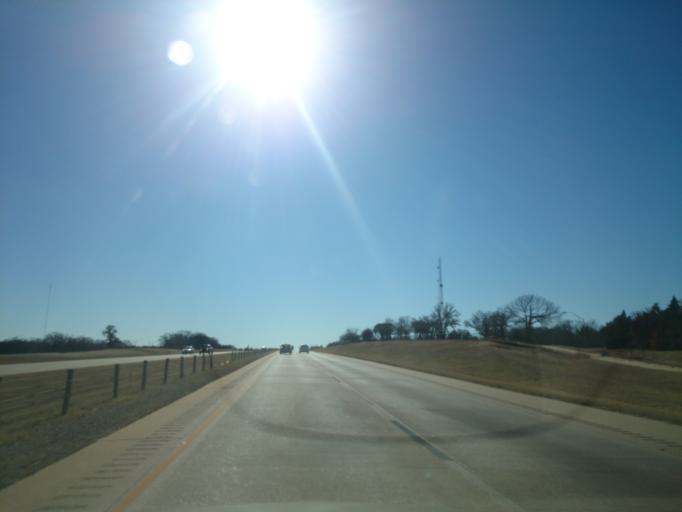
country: US
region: Oklahoma
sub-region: Logan County
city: Guthrie
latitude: 35.7631
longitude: -97.4164
